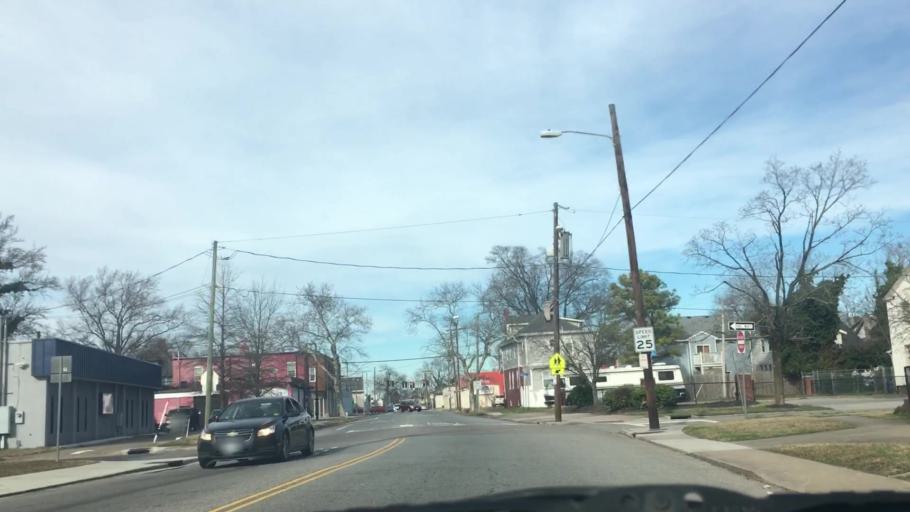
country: US
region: Virginia
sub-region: City of Norfolk
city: Norfolk
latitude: 36.8761
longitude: -76.2948
